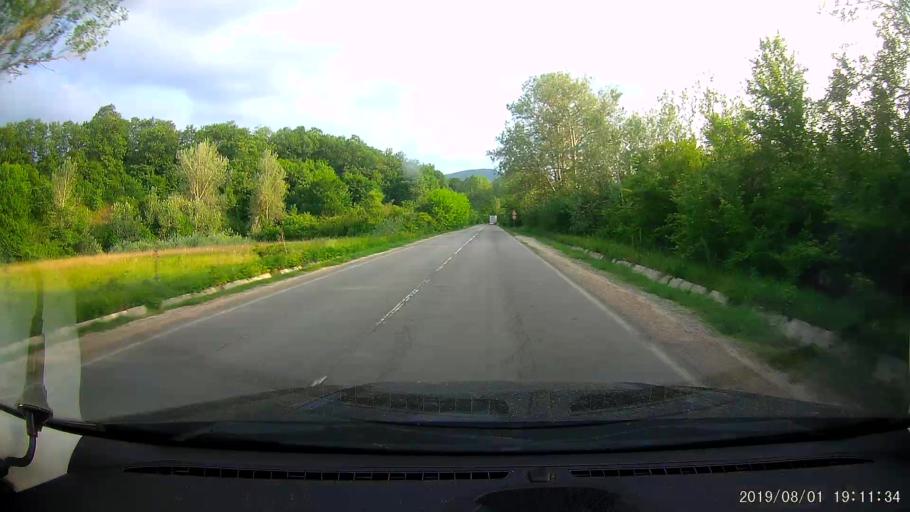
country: BG
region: Shumen
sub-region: Obshtina Smyadovo
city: Smyadovo
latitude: 42.9725
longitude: 26.9599
